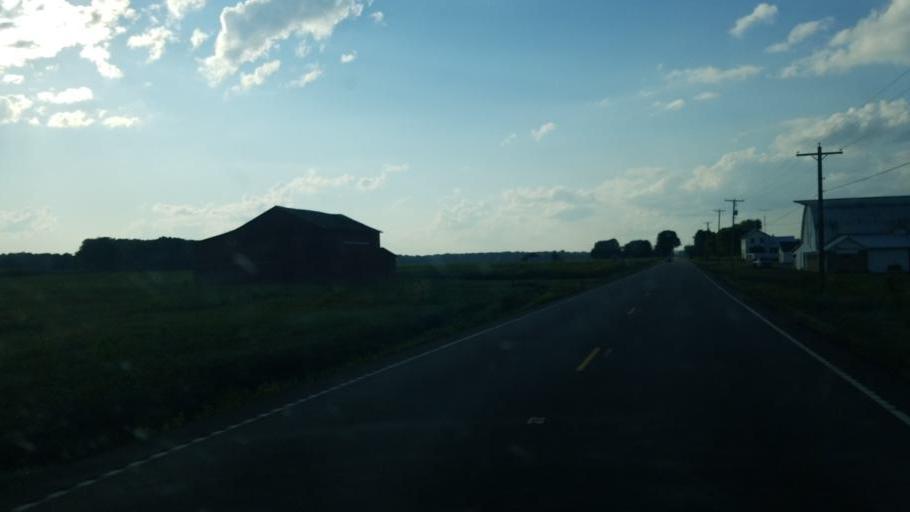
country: US
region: Ohio
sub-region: Knox County
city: Fredericktown
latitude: 40.4428
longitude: -82.5270
